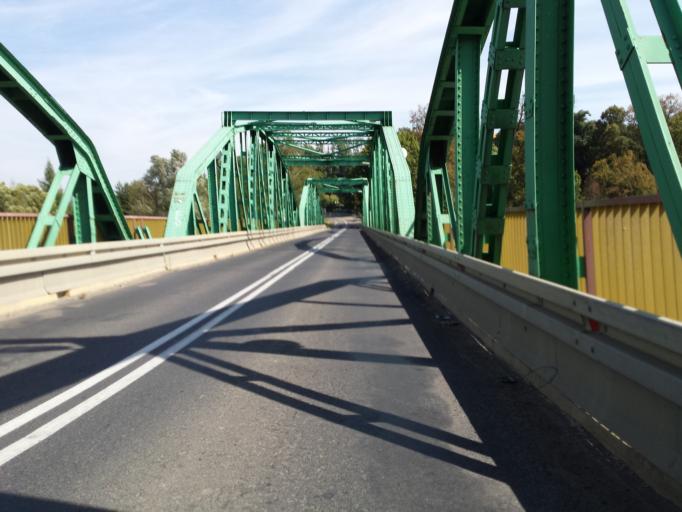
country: PL
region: Subcarpathian Voivodeship
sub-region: Powiat leski
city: Lesko
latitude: 49.4685
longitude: 22.3212
